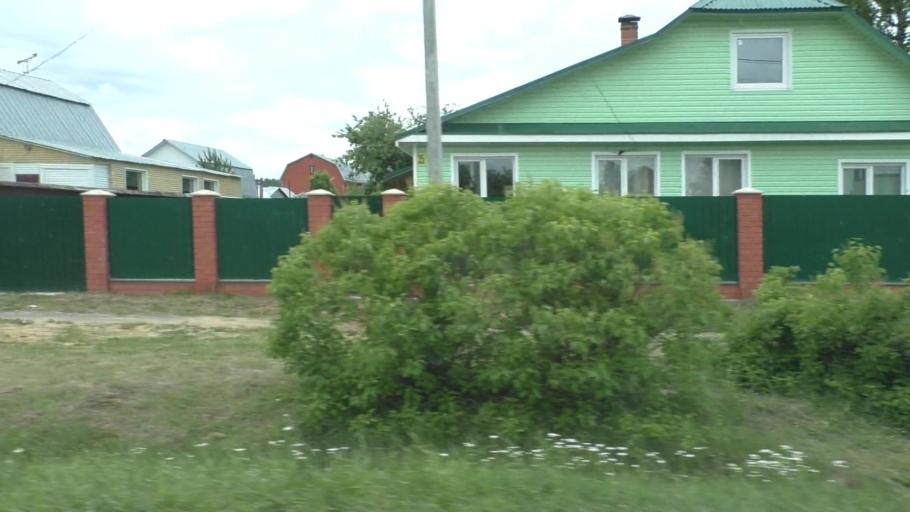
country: RU
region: Moskovskaya
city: Il'inskiy Pogost
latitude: 55.5022
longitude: 38.7952
